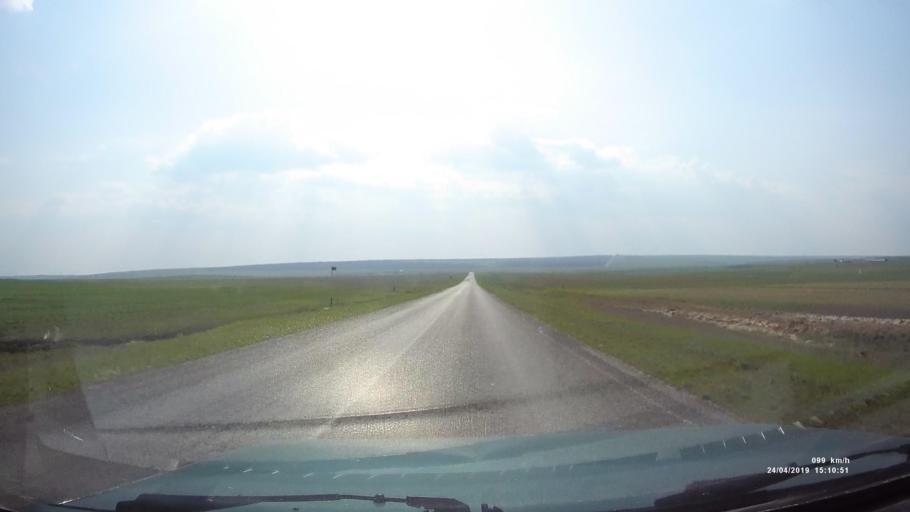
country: RU
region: Rostov
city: Remontnoye
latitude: 46.5469
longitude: 43.3330
